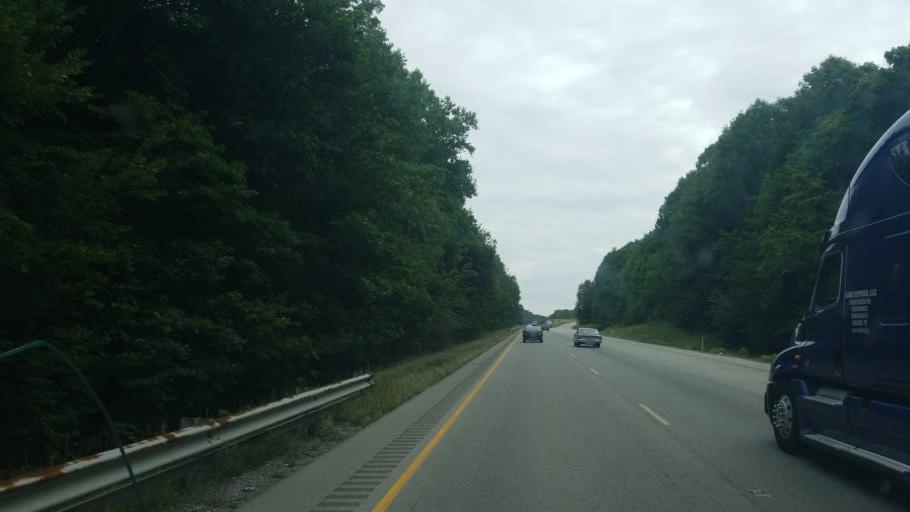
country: US
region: Indiana
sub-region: Putnam County
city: Cloverdale
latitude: 39.5234
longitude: -86.8848
